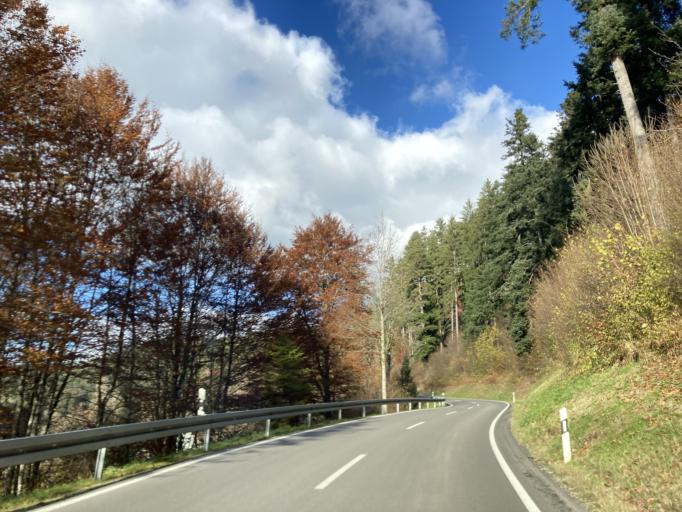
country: DE
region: Baden-Wuerttemberg
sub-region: Freiburg Region
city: Dornhan
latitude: 48.3500
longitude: 8.4956
